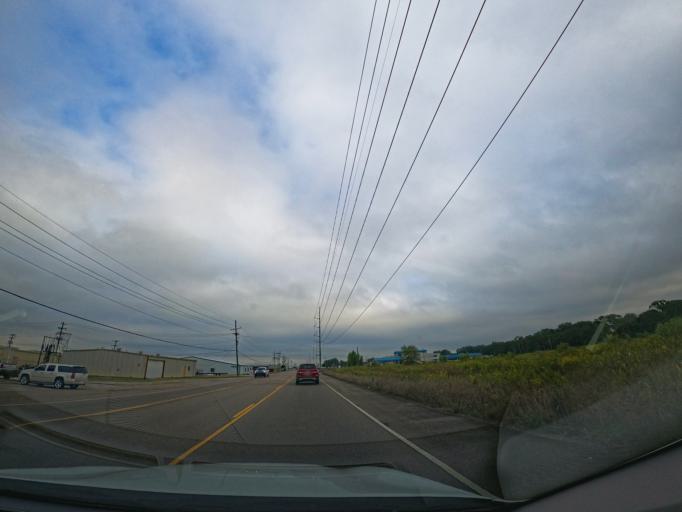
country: US
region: Louisiana
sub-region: Terrebonne Parish
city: Presquille
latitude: 29.5492
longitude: -90.6791
